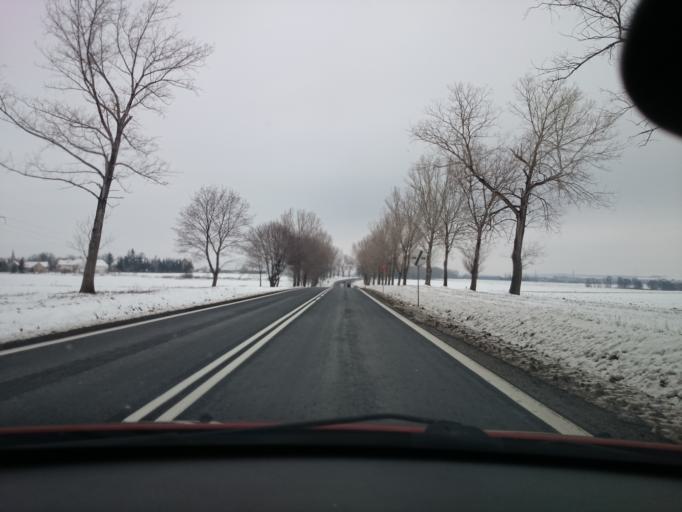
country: PL
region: Lower Silesian Voivodeship
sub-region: Powiat zabkowicki
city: Zabkowice Slaskie
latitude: 50.5691
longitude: 16.7899
